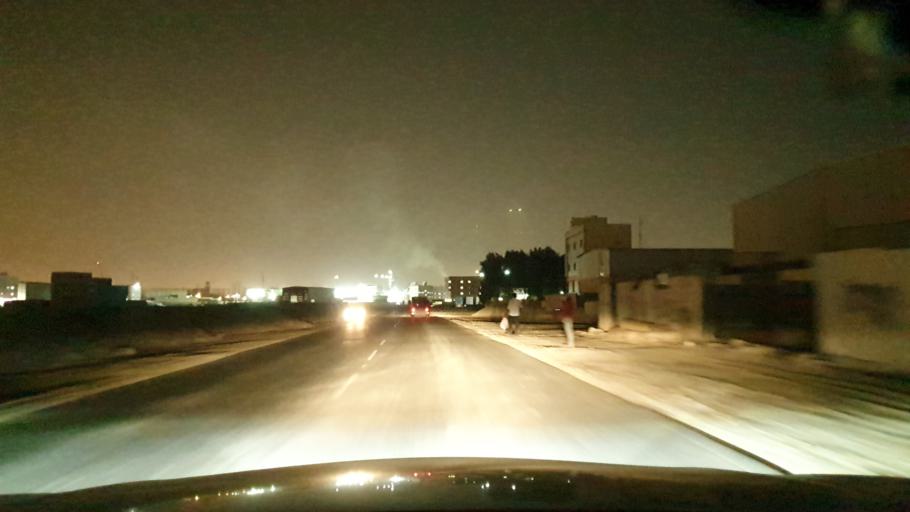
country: BH
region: Northern
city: Sitrah
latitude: 26.0915
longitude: 50.6157
